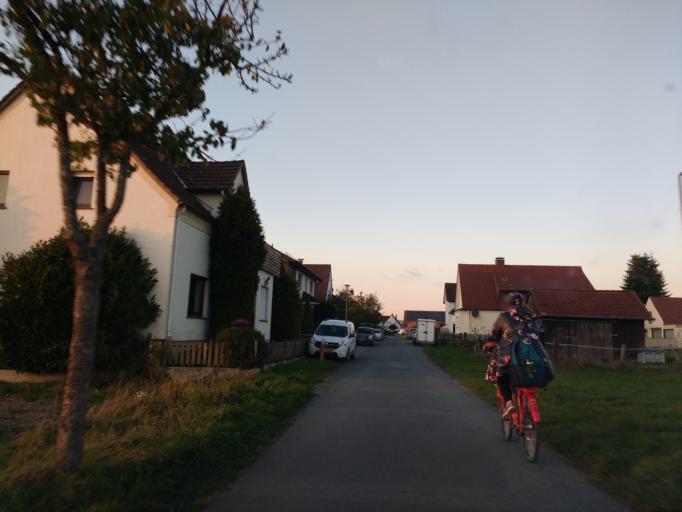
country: DE
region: North Rhine-Westphalia
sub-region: Regierungsbezirk Detmold
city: Schlangen
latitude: 51.8052
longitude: 8.8472
